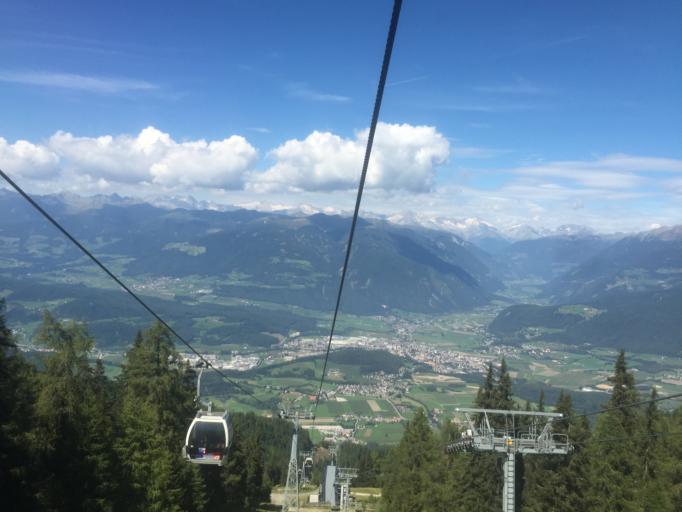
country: IT
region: Trentino-Alto Adige
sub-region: Bolzano
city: Riscone
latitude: 46.7464
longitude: 11.9536
